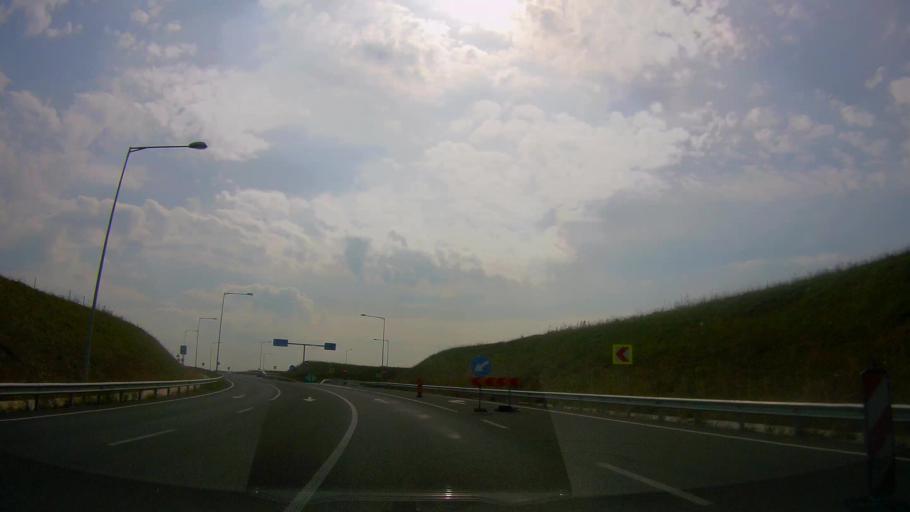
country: RO
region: Cluj
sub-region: Comuna Baciu
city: Mera
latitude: 46.8113
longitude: 23.4199
